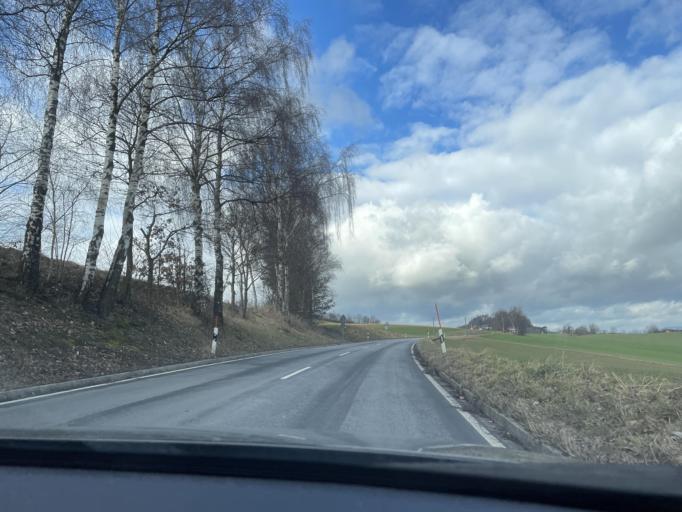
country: DE
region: Bavaria
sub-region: Upper Palatinate
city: Runding
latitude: 49.2063
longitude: 12.7716
